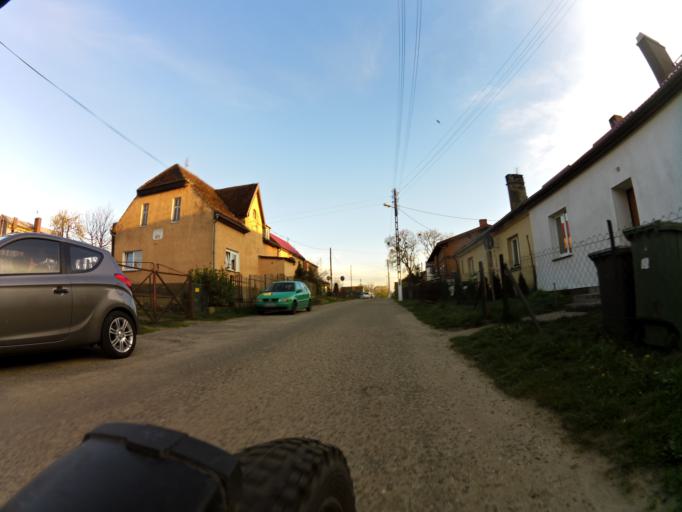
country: PL
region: West Pomeranian Voivodeship
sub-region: Powiat lobeski
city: Lobez
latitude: 53.7003
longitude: 15.6463
